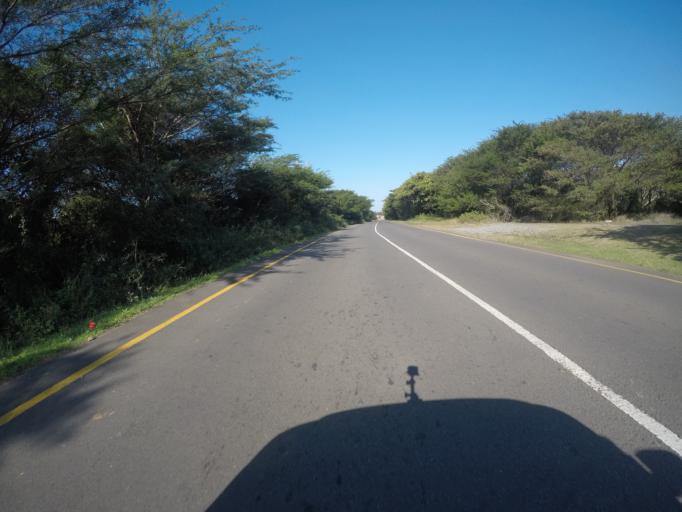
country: ZA
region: KwaZulu-Natal
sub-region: uThungulu District Municipality
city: Richards Bay
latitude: -28.7847
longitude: 32.0776
